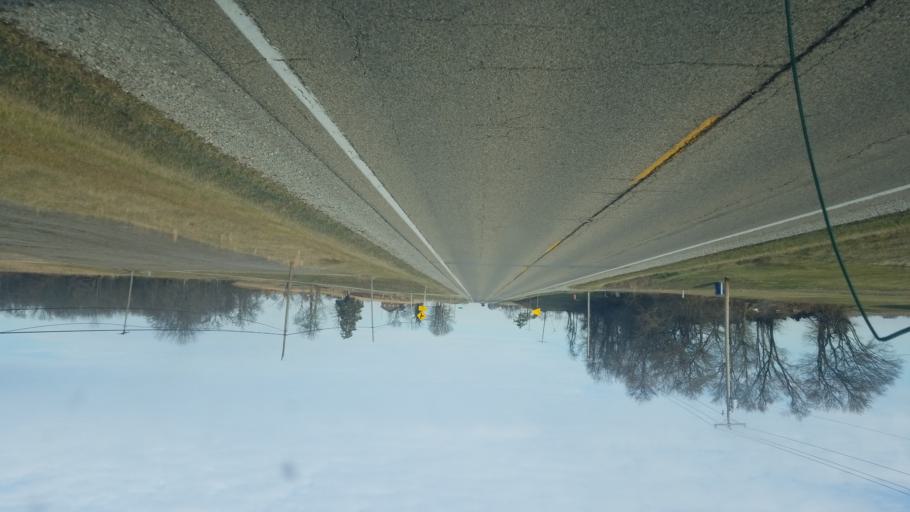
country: US
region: Illinois
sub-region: Lawrence County
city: Bridgeport
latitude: 38.6084
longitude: -87.6943
